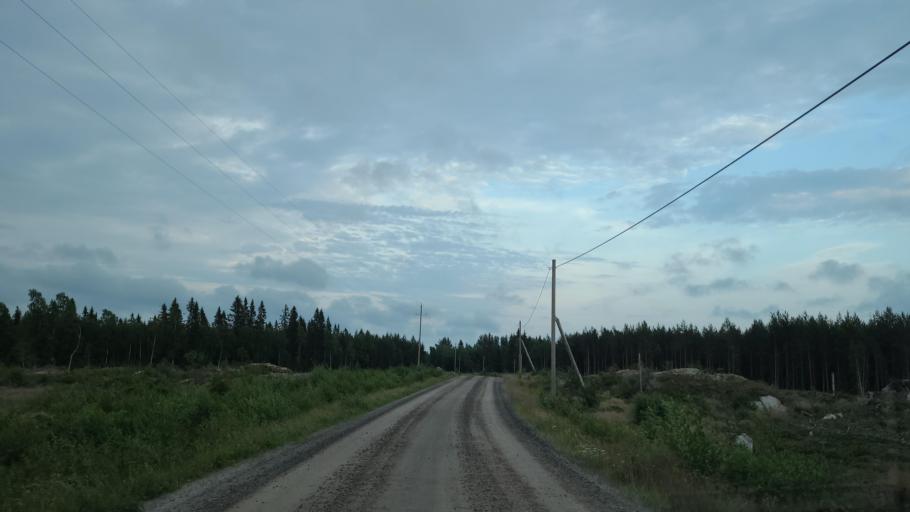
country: FI
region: Ostrobothnia
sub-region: Vaasa
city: Replot
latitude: 63.3179
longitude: 21.1521
